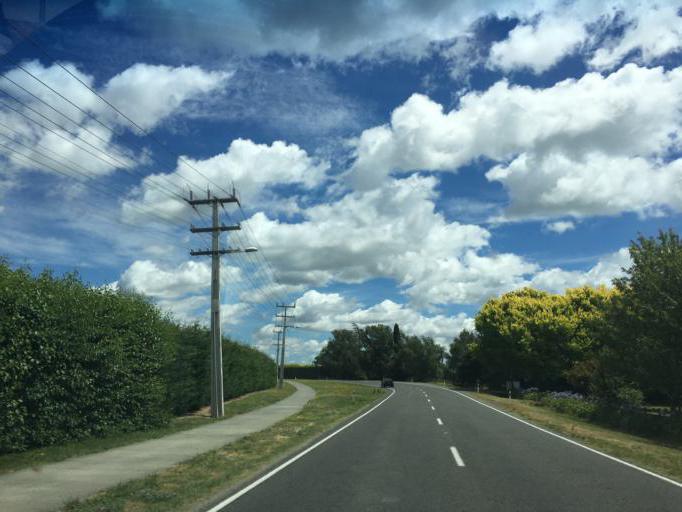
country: NZ
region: Hawke's Bay
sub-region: Hastings District
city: Hastings
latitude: -39.6569
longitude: 176.8804
